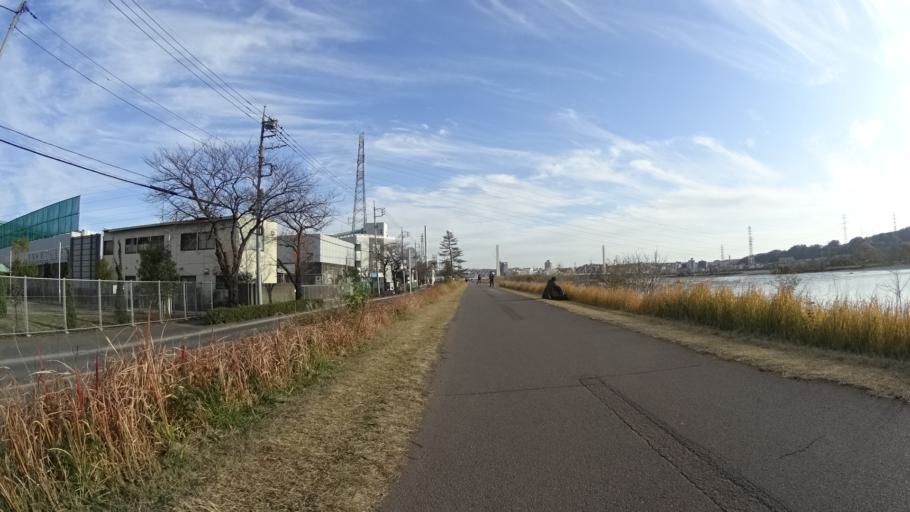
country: JP
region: Tokyo
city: Hino
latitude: 35.6666
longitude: 139.4352
